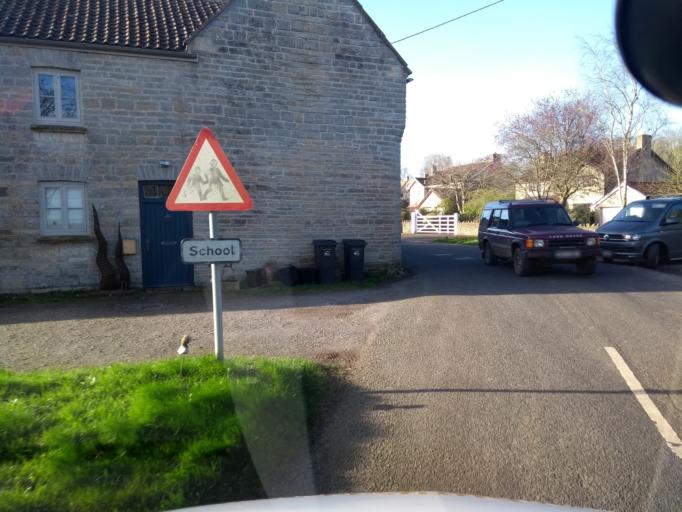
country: GB
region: England
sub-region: Somerset
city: Wedmore
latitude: 51.1433
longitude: -2.8330
